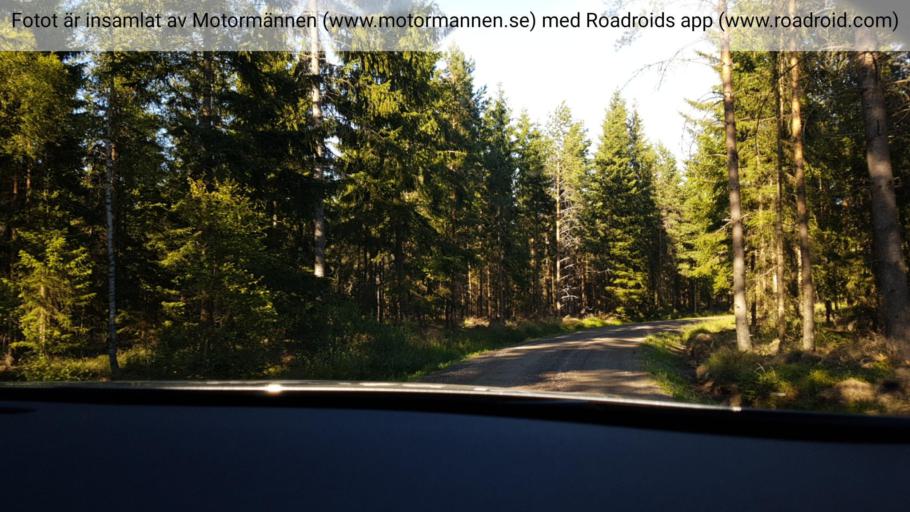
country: SE
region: Joenkoeping
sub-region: Vaggeryds Kommun
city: Skillingaryd
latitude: 57.3746
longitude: 14.0381
